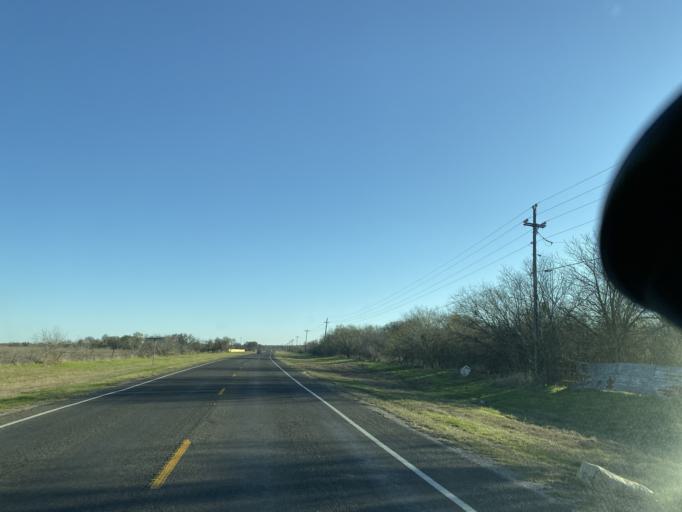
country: US
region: Texas
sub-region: Bastrop County
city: Wyldwood
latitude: 30.0970
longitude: -97.5052
